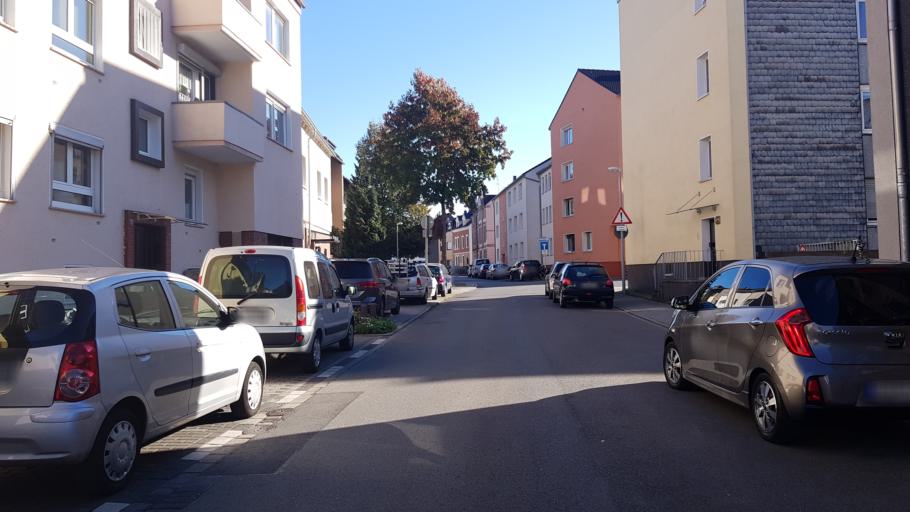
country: DE
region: North Rhine-Westphalia
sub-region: Regierungsbezirk Dusseldorf
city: Muelheim (Ruhr)
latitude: 51.4281
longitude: 6.8528
